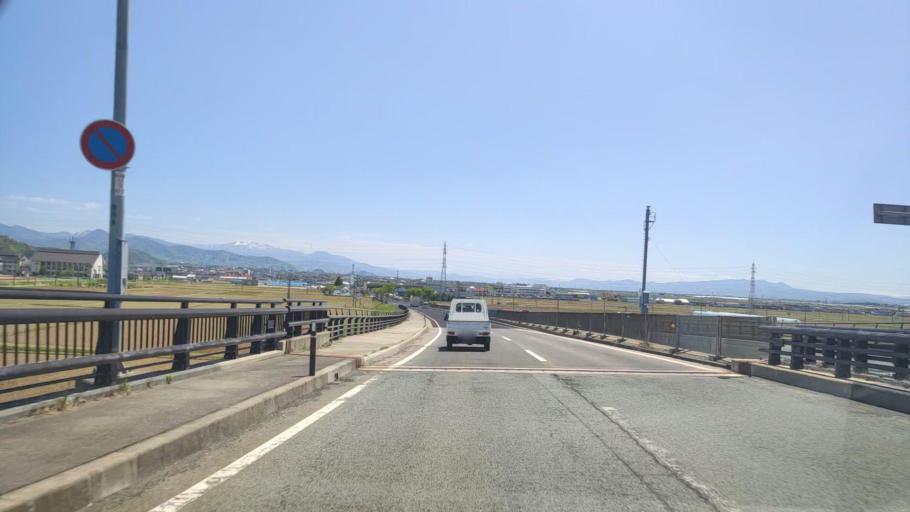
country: JP
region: Yamagata
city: Higashine
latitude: 38.4925
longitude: 140.3835
